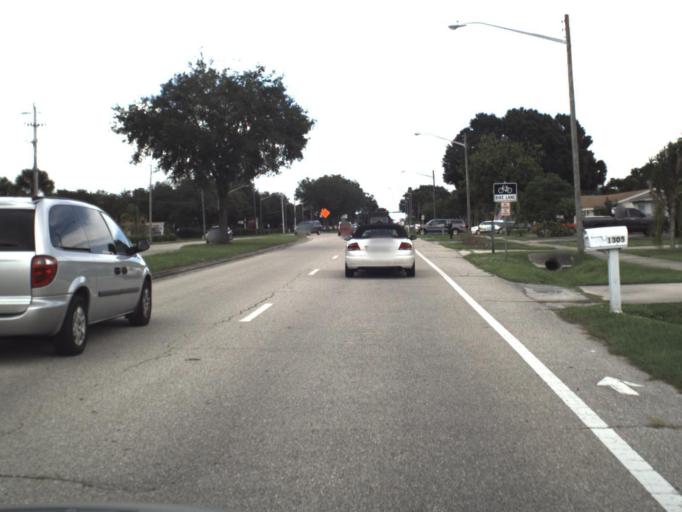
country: US
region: Florida
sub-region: Sarasota County
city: Venice Gardens
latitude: 27.0997
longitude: -82.4208
